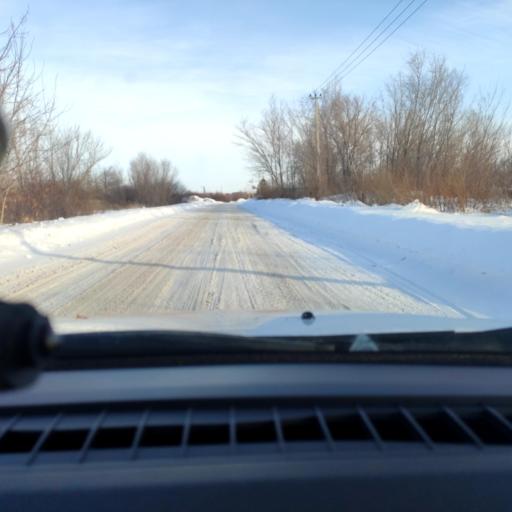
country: RU
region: Samara
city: Chapayevsk
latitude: 52.9928
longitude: 49.7388
